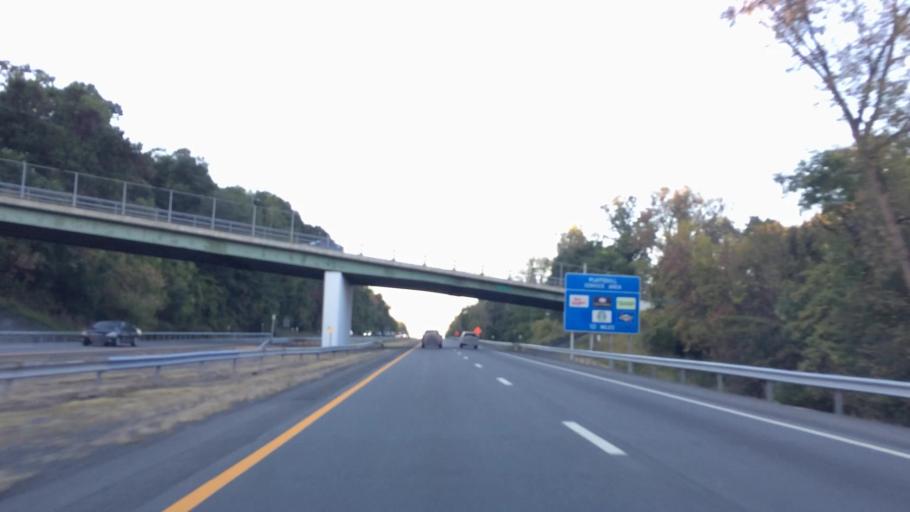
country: US
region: New York
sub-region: Orange County
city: Firthcliffe
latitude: 41.4290
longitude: -74.0681
